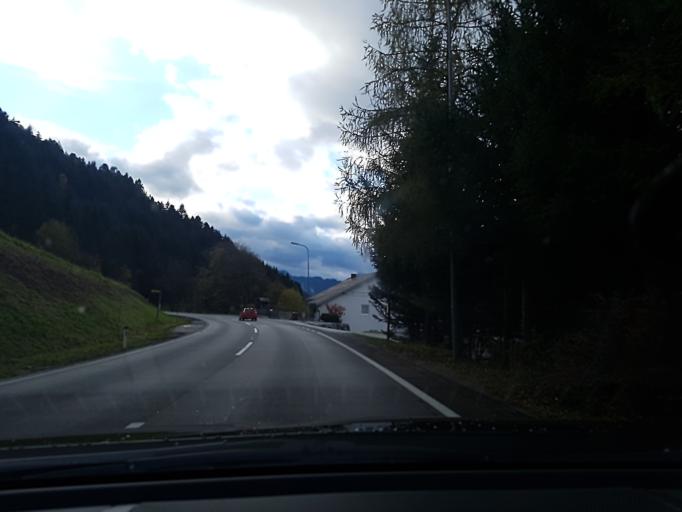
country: AT
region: Styria
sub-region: Politischer Bezirk Liezen
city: Liezen
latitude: 47.5513
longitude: 14.2566
